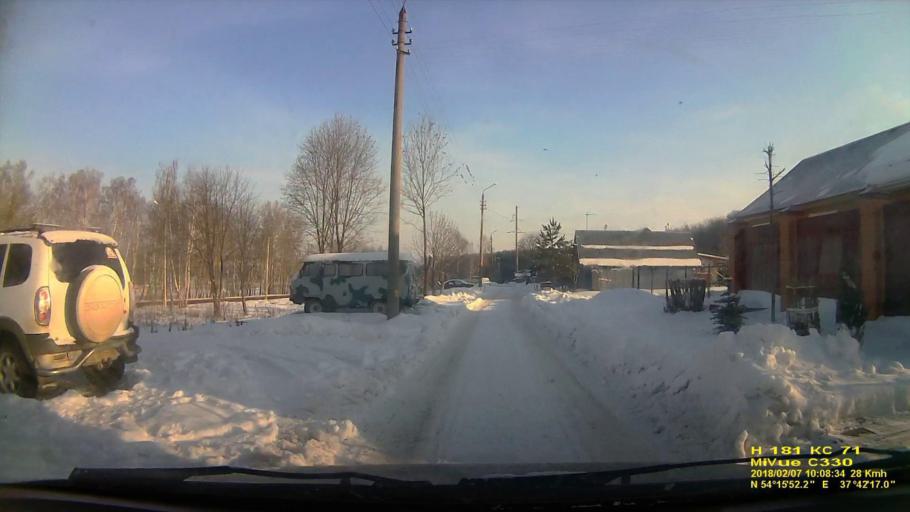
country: RU
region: Tula
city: Gorelki
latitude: 54.2646
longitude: 37.7049
